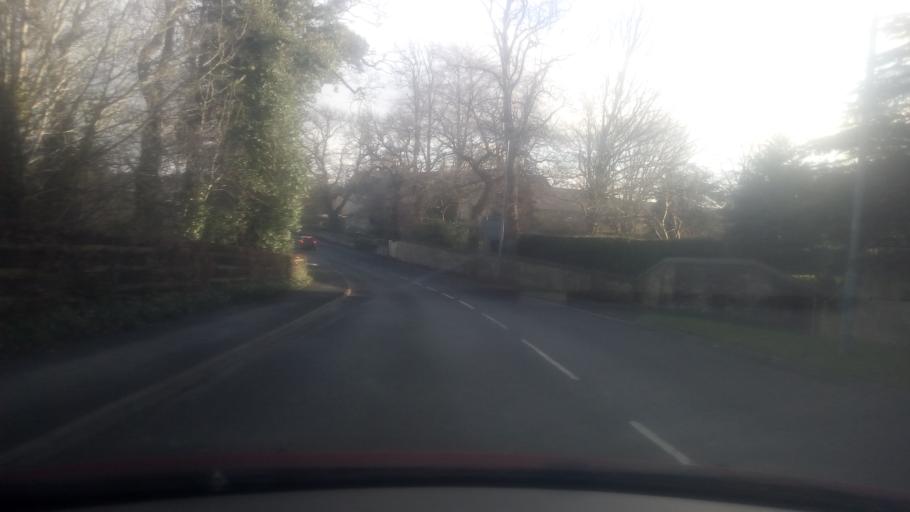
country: GB
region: Scotland
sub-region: The Scottish Borders
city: Kelso
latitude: 55.6029
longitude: -2.4282
